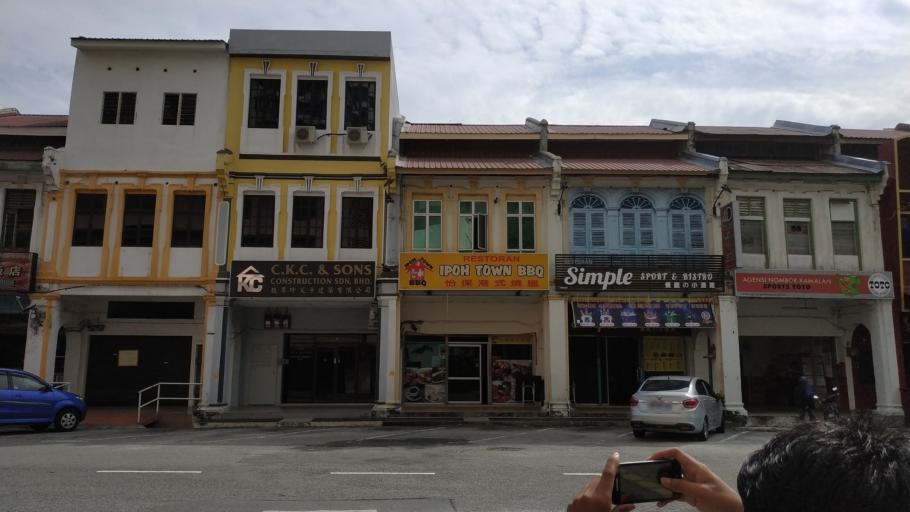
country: MY
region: Perak
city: Ipoh
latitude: 4.5922
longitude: 101.0831
